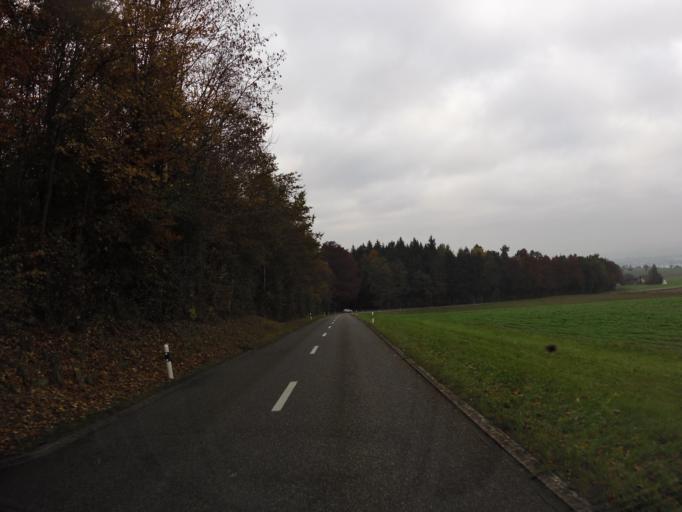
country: CH
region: Thurgau
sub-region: Kreuzlingen District
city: Ermatingen
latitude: 47.6520
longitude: 9.0993
